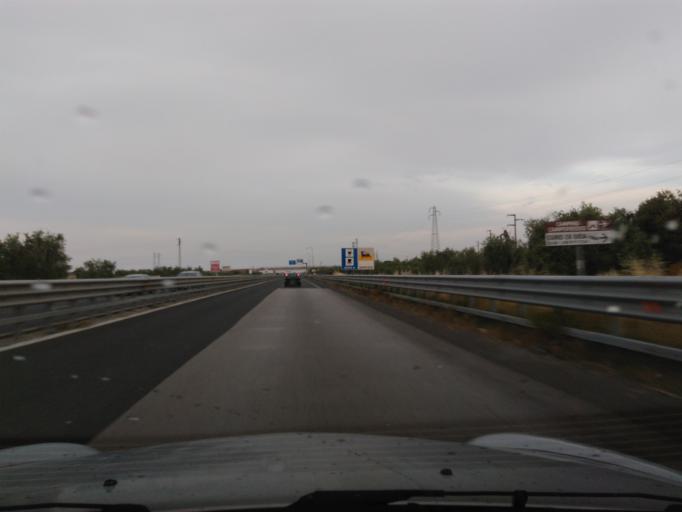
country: IT
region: Apulia
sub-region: Provincia di Bari
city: Giovinazzo
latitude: 41.1740
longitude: 16.6673
